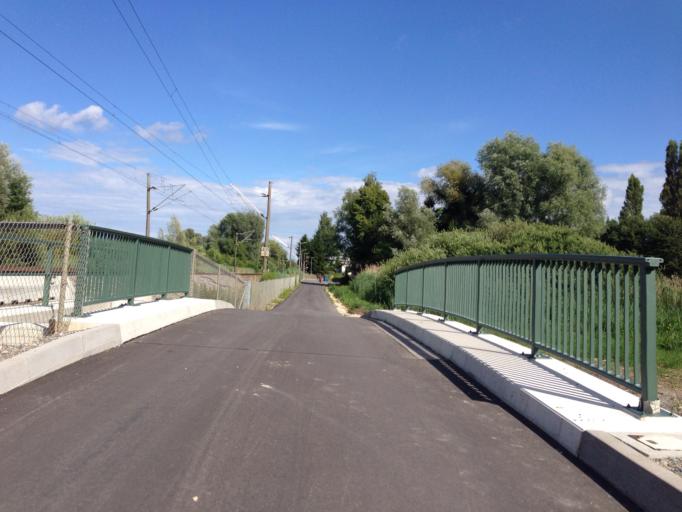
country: CH
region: Thurgau
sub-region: Kreuzlingen District
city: Gottlieben
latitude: 47.6871
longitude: 9.1325
